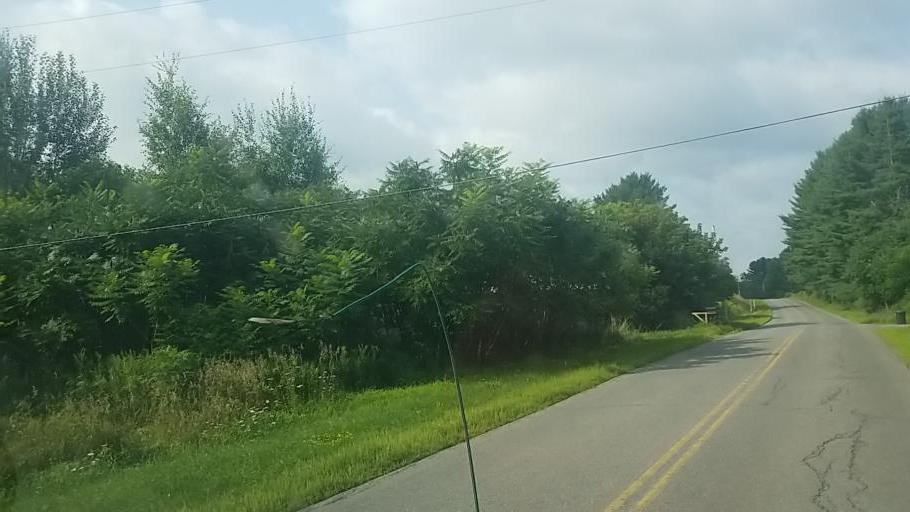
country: US
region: New York
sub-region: Fulton County
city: Broadalbin
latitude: 43.0718
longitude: -74.2376
